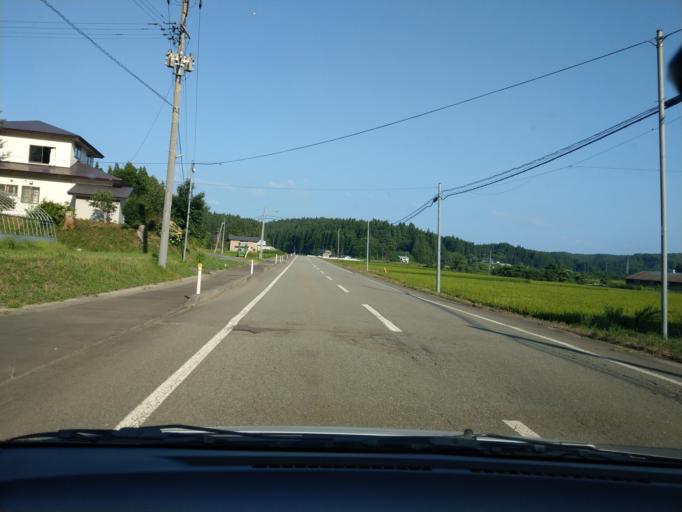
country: JP
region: Akita
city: Akita
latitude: 39.6035
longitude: 140.2238
